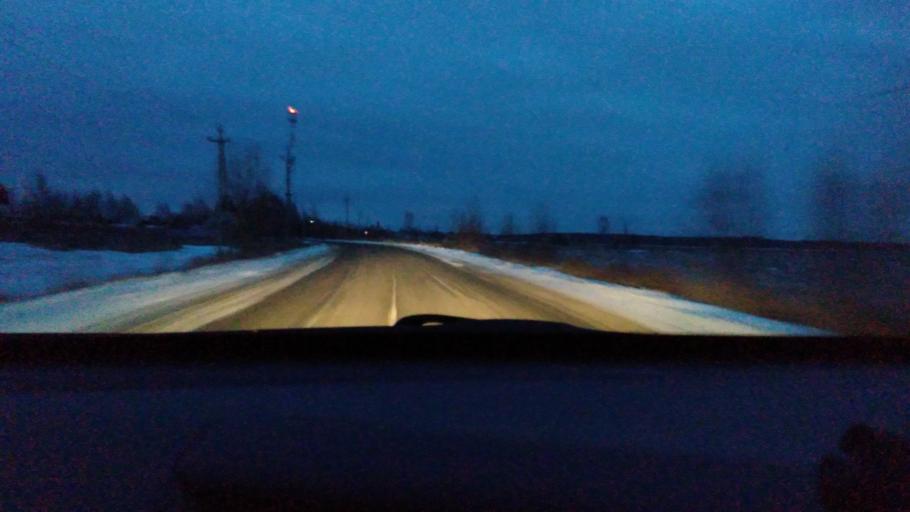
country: RU
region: Moskovskaya
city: Meshcherino
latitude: 55.2941
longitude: 38.3428
